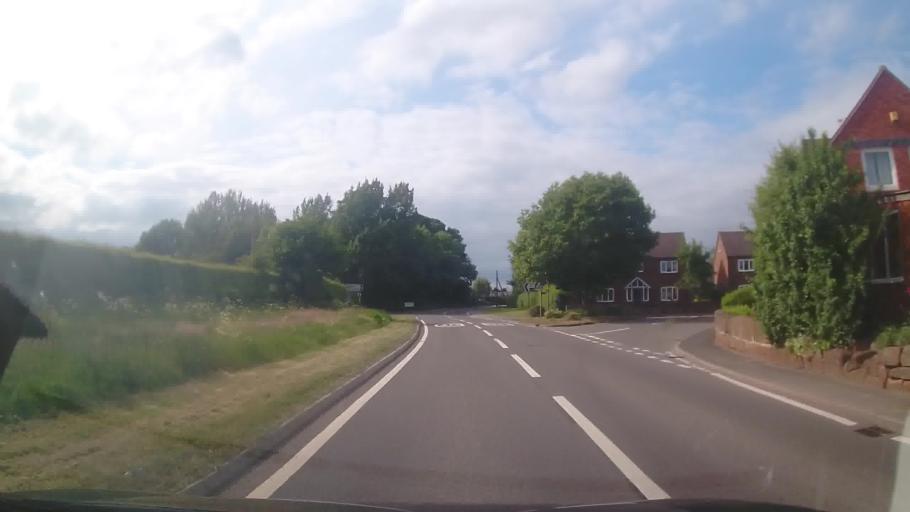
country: GB
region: England
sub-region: Shropshire
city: Petton
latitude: 52.8283
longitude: -2.8061
